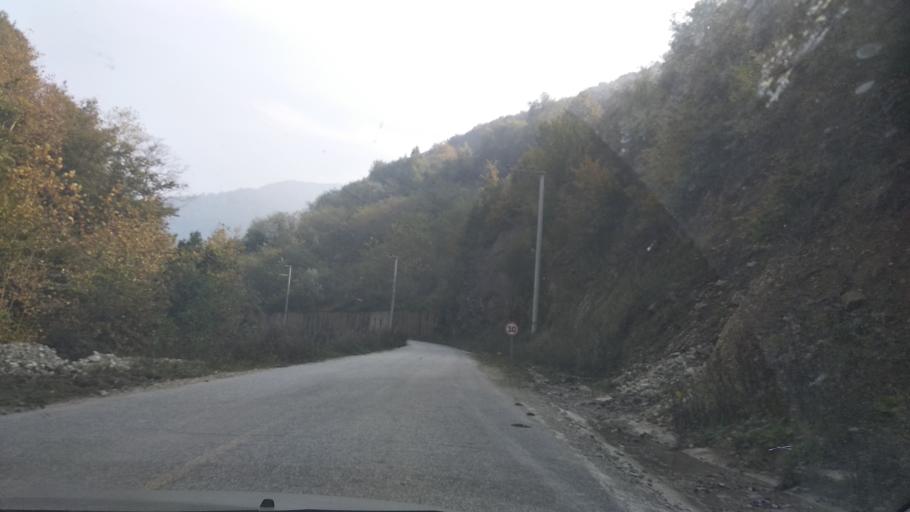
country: TR
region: Duzce
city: Kaynasli
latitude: 40.7319
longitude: 31.2272
